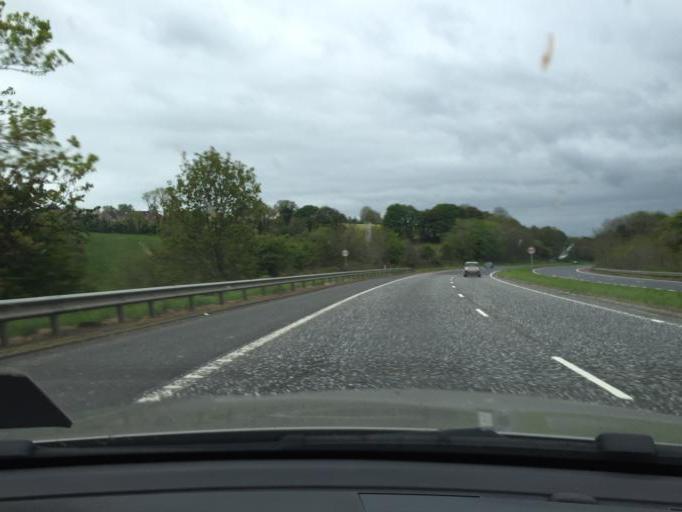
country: GB
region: Northern Ireland
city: Hillsborough
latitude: 54.4239
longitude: -6.1216
